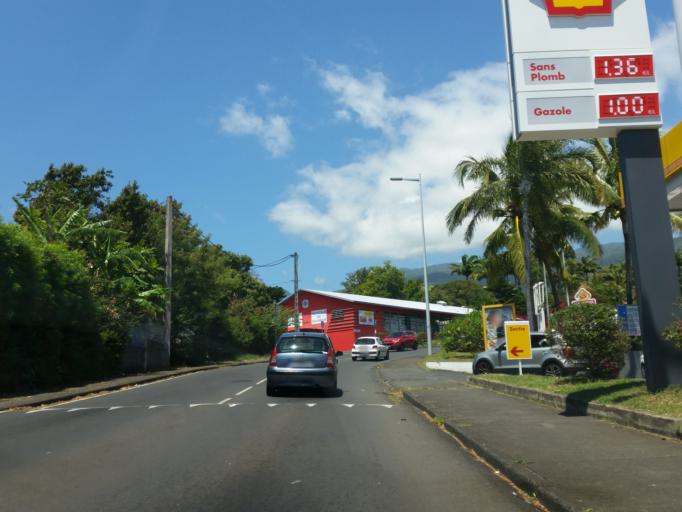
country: RE
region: Reunion
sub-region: Reunion
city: Saint-Denis
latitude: -20.9035
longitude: 55.4920
